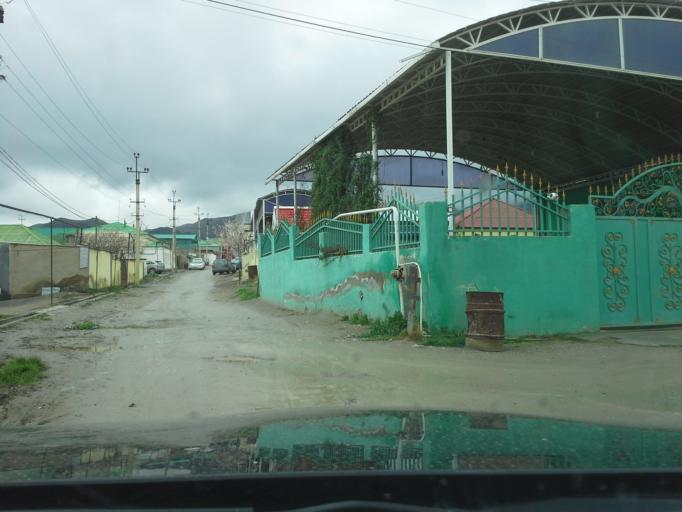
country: TM
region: Ahal
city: Abadan
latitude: 37.9570
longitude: 58.2107
